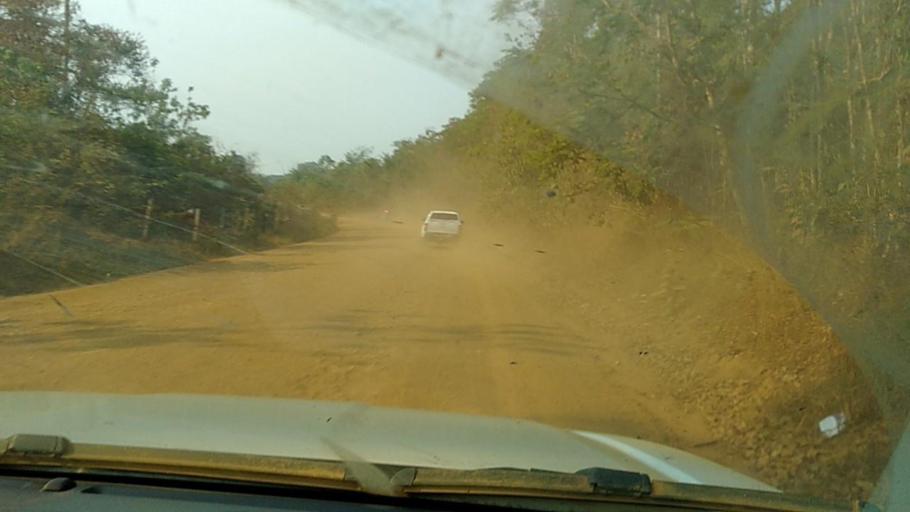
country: BR
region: Rondonia
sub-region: Porto Velho
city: Porto Velho
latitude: -8.7467
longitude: -63.9648
